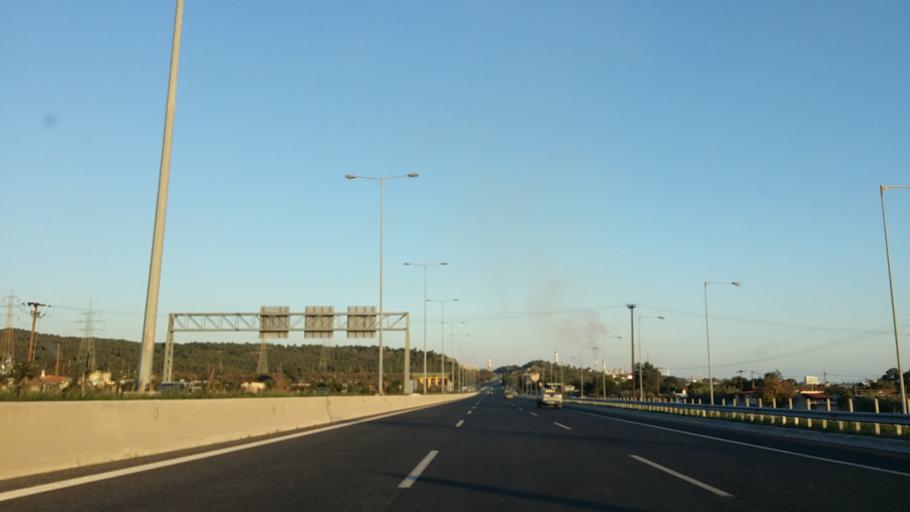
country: GR
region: Peloponnese
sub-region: Nomos Korinthias
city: Isthmia
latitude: 37.9253
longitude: 23.0381
